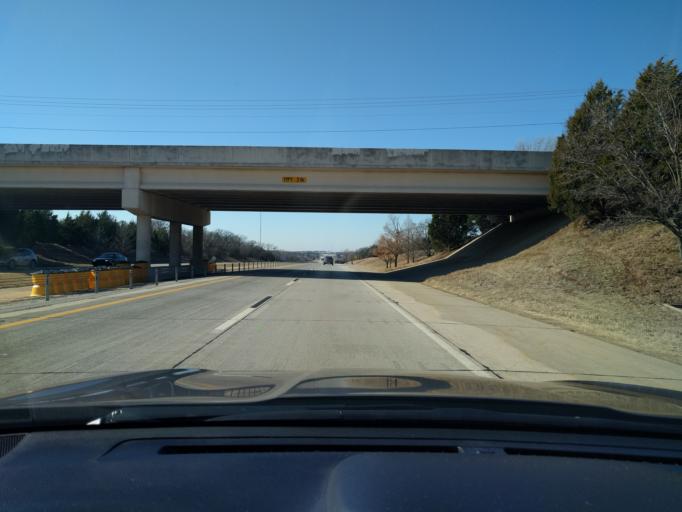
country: US
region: Oklahoma
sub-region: Oklahoma County
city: Edmond
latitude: 35.6014
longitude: -97.4600
